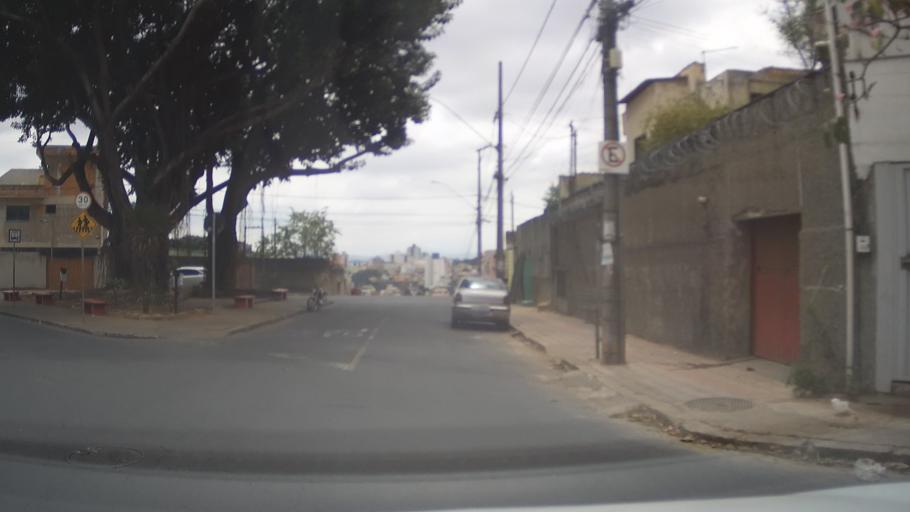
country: BR
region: Minas Gerais
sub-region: Belo Horizonte
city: Belo Horizonte
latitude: -19.9015
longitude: -43.9419
